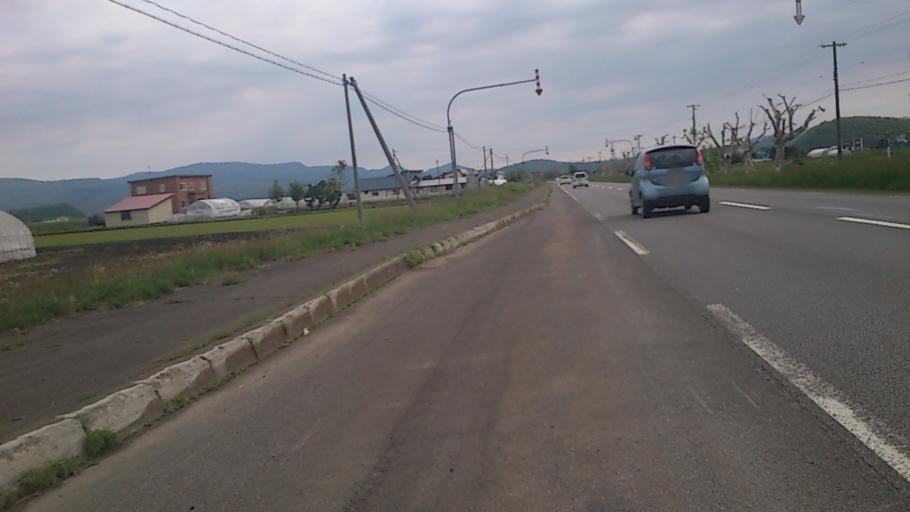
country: JP
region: Hokkaido
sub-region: Asahikawa-shi
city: Asahikawa
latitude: 43.8591
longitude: 142.5104
